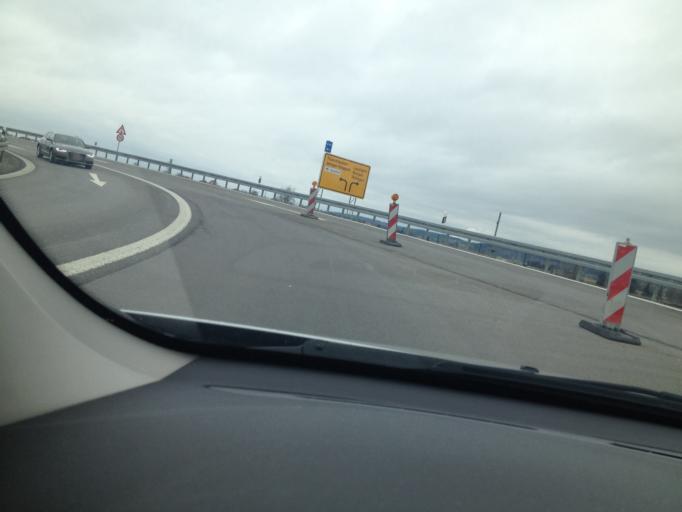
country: DE
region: Bavaria
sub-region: Swabia
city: Rofingen
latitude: 48.4136
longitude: 10.4381
